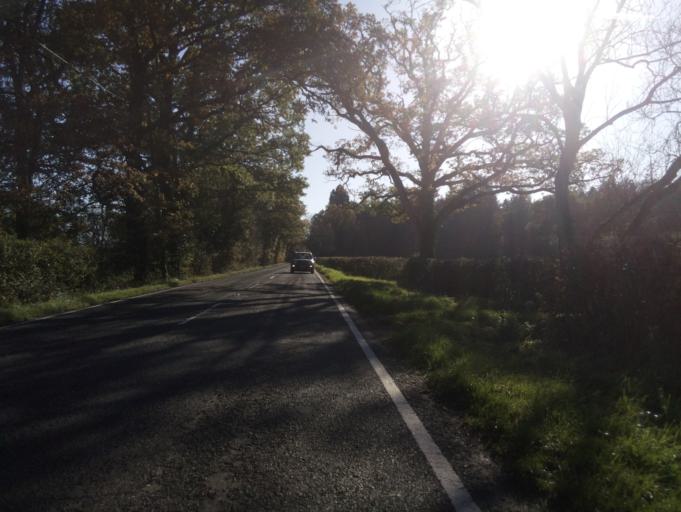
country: GB
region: England
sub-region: Dorset
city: Sherborne
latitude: 50.8718
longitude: -2.4799
